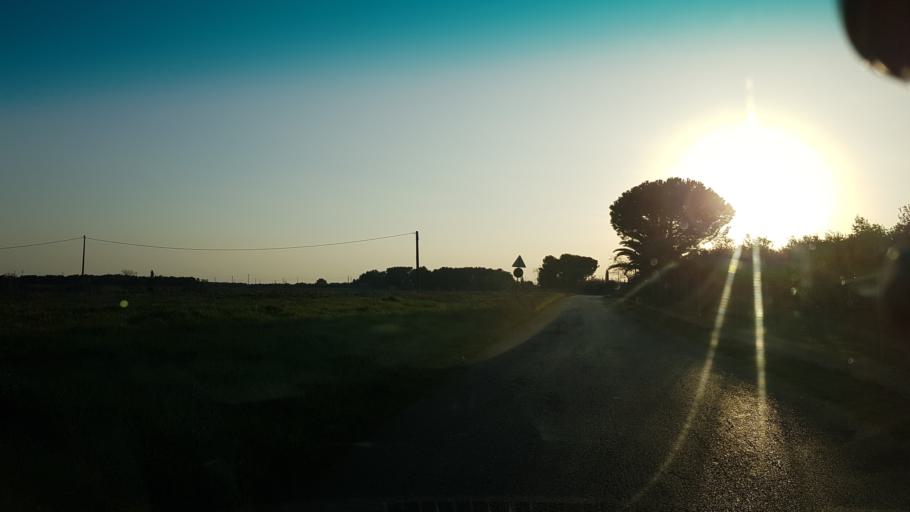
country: IT
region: Apulia
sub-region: Provincia di Brindisi
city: Mesagne
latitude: 40.5528
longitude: 17.8004
